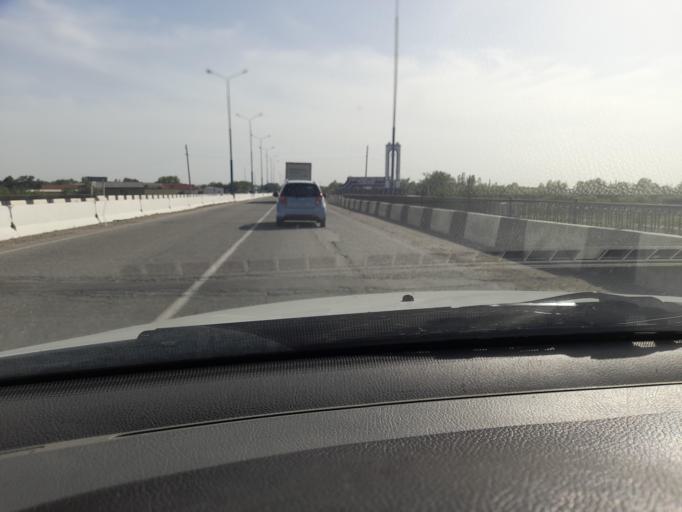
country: UZ
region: Samarqand
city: Kattaqo'rg'on
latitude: 39.9276
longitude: 66.3598
